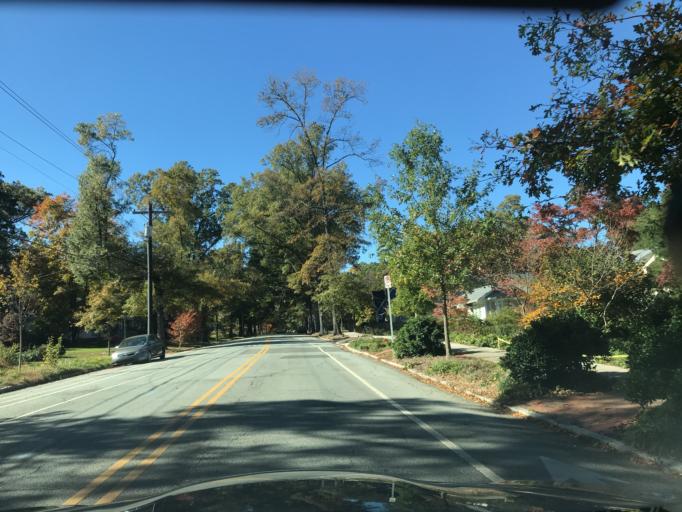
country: US
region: North Carolina
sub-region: Durham County
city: Durham
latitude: 36.0176
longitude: -78.9296
